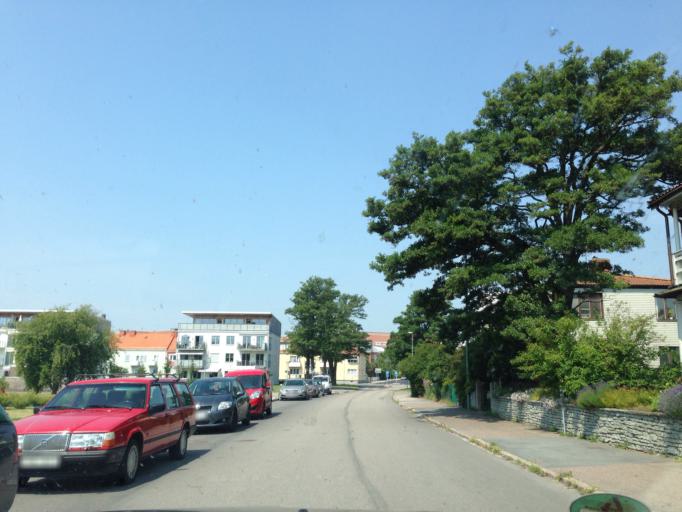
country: SE
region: Kalmar
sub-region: Kalmar Kommun
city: Kalmar
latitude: 56.6547
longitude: 16.3371
